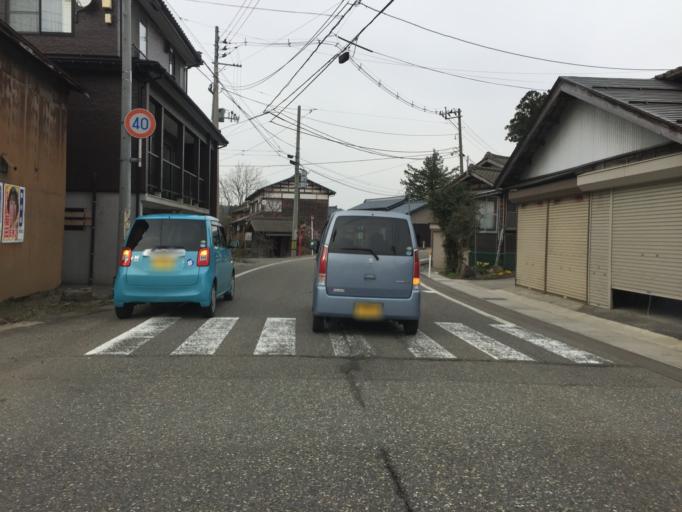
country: JP
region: Niigata
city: Tochio-honcho
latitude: 37.4980
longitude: 139.0205
